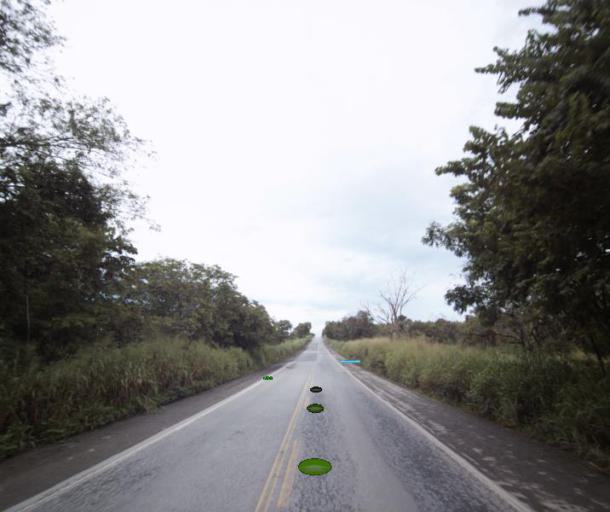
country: BR
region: Goias
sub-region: Porangatu
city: Porangatu
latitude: -13.5028
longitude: -49.1282
